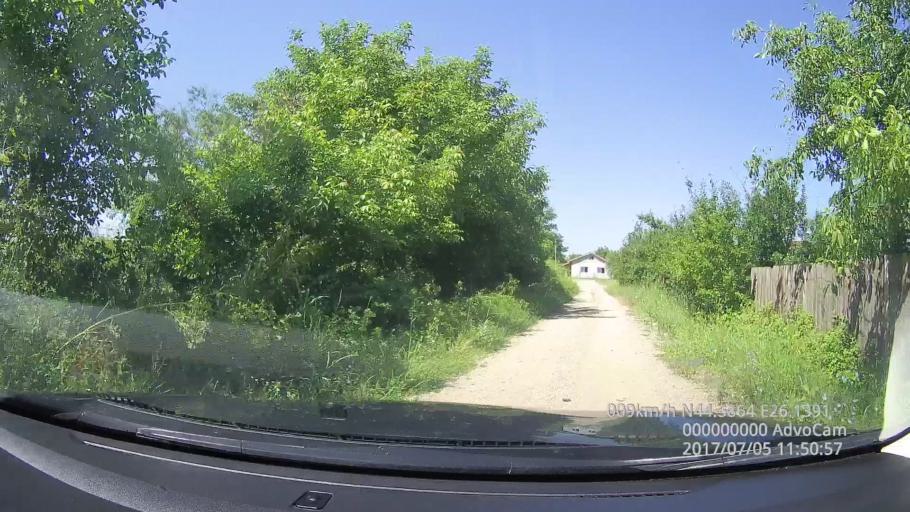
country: RO
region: Ilfov
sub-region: Comuna Tunari
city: Tunari
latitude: 44.5861
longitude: 26.1390
